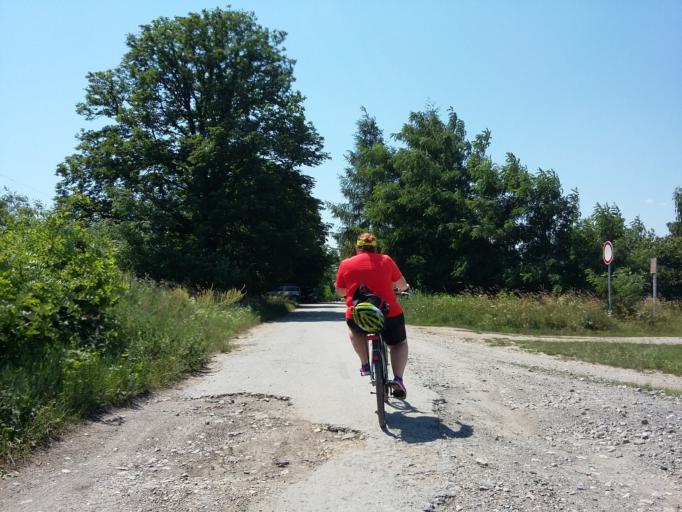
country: AT
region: Lower Austria
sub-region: Politischer Bezirk Ganserndorf
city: Marchegg
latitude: 48.2740
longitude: 16.9647
